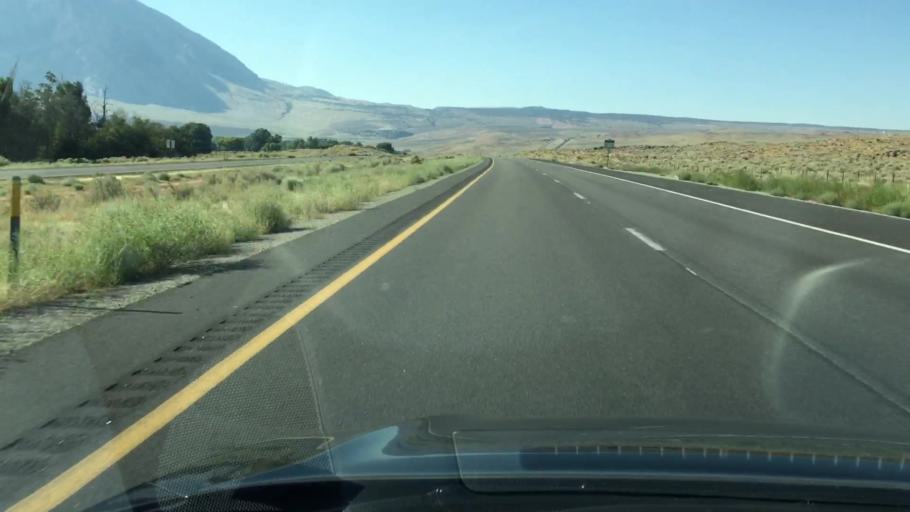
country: US
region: California
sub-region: Inyo County
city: West Bishop
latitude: 37.4220
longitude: -118.5566
